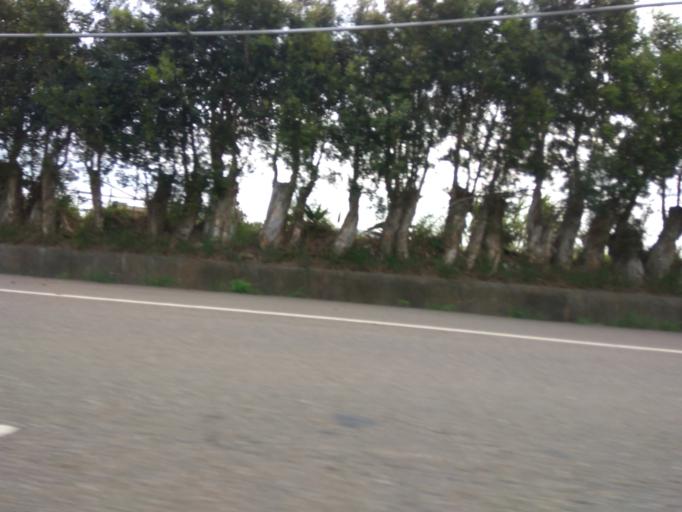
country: TW
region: Taiwan
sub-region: Hsinchu
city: Zhubei
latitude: 24.9696
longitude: 121.0217
